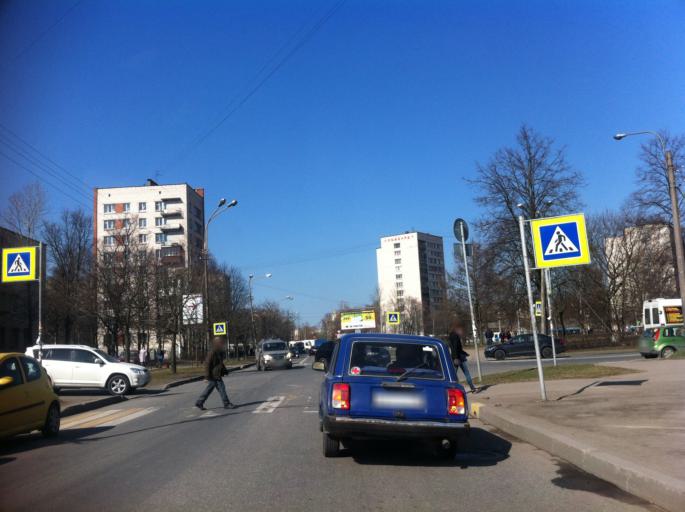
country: RU
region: St.-Petersburg
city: Dachnoye
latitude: 59.8410
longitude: 30.2464
